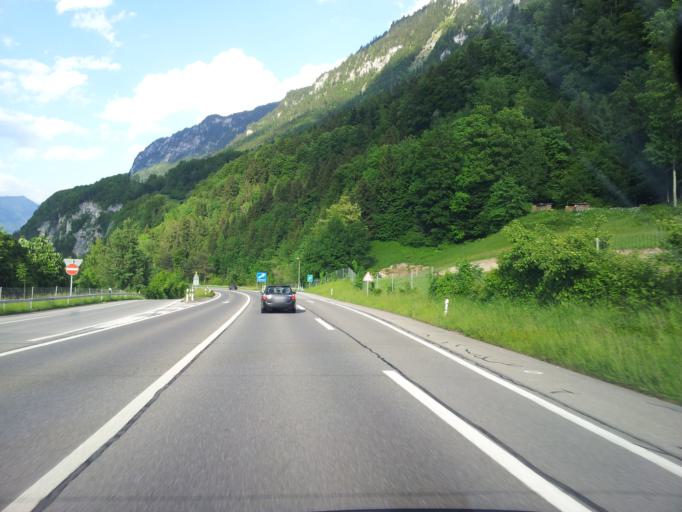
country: CH
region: Bern
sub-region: Interlaken-Oberhasli District
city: Ringgenberg
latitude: 46.7063
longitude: 7.9595
